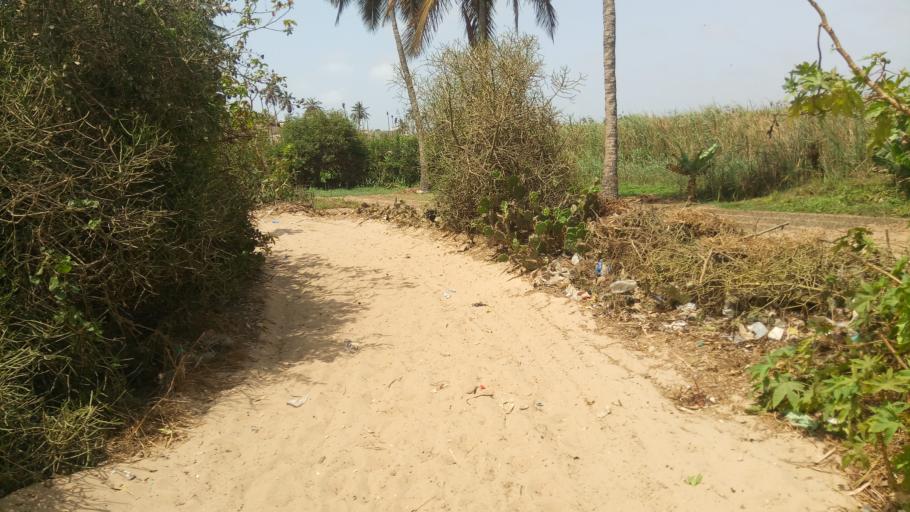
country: SN
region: Dakar
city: Pikine
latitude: 14.7962
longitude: -17.3386
